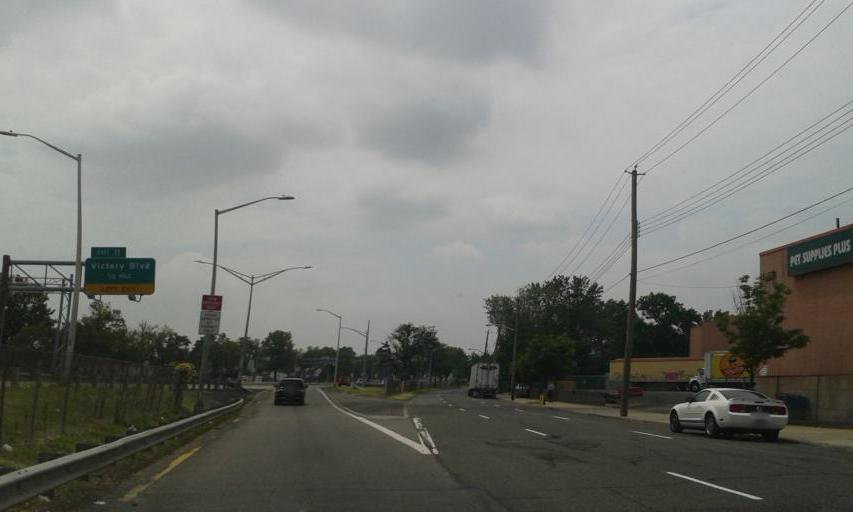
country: US
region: New York
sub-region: Richmond County
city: Bloomfield
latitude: 40.6234
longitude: -74.1474
